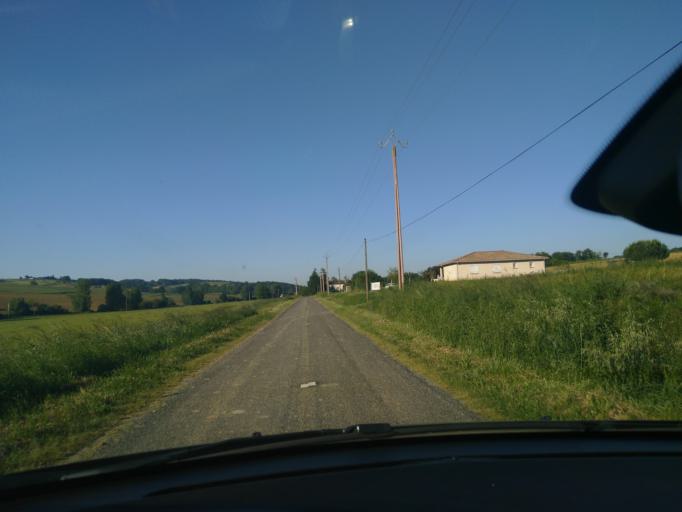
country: FR
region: Midi-Pyrenees
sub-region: Departement du Tarn-et-Garonne
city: Beaumont-de-Lomagne
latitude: 43.8144
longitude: 1.0395
